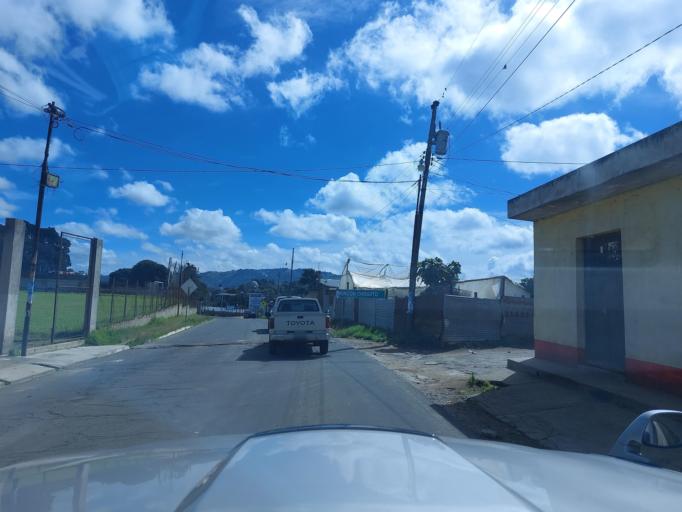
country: GT
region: Chimaltenango
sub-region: Municipio de Zaragoza
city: Zaragoza
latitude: 14.6734
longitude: -90.8983
